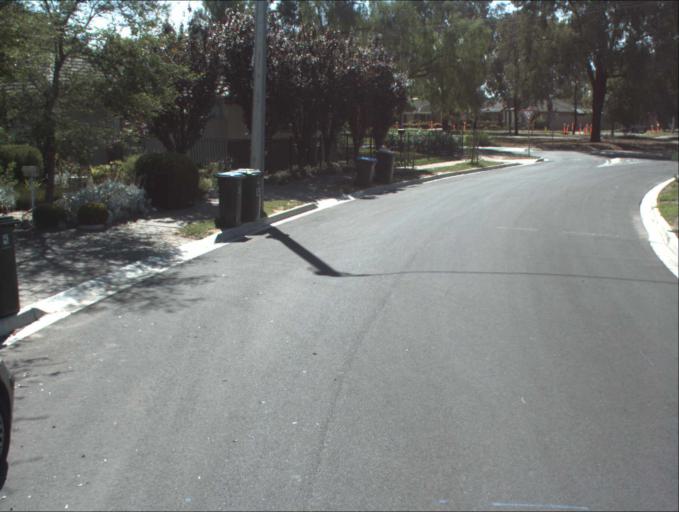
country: AU
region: South Australia
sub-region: Port Adelaide Enfield
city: Gilles Plains
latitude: -34.8596
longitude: 138.6483
